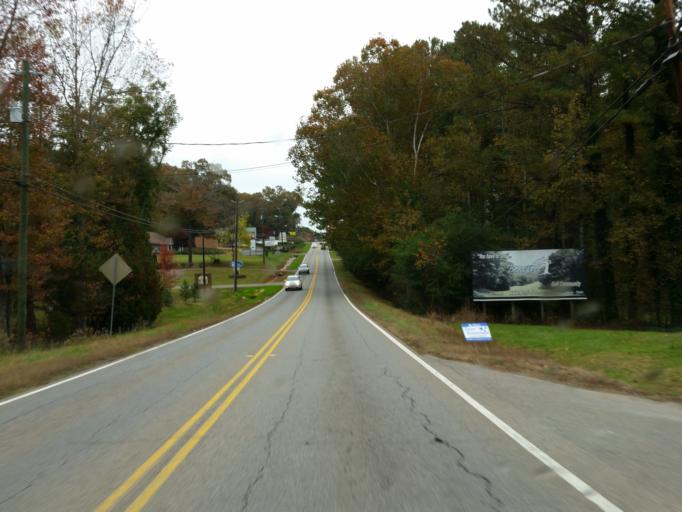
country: US
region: Georgia
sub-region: Pickens County
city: Jasper
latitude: 34.4658
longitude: -84.4446
